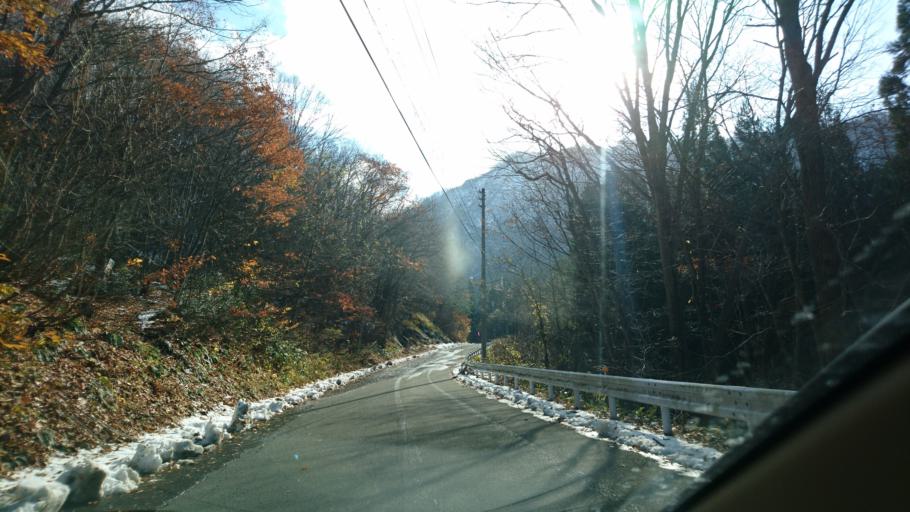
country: JP
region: Iwate
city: Kitakami
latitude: 39.2937
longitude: 140.8444
